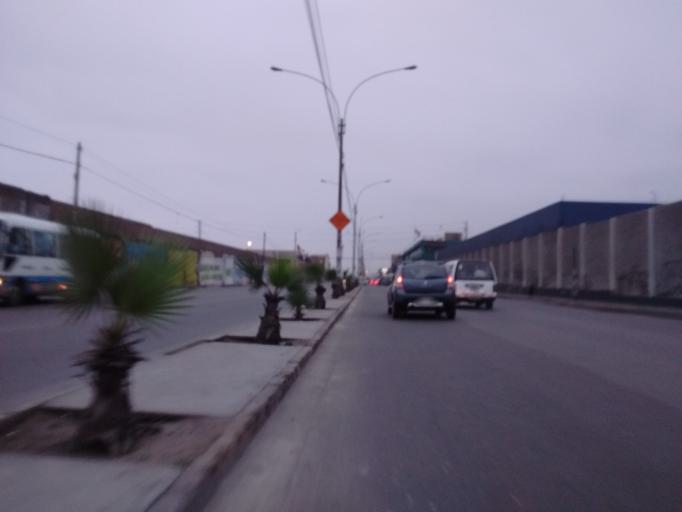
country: PE
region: Callao
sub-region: Callao
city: Callao
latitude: -12.0456
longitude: -77.0767
